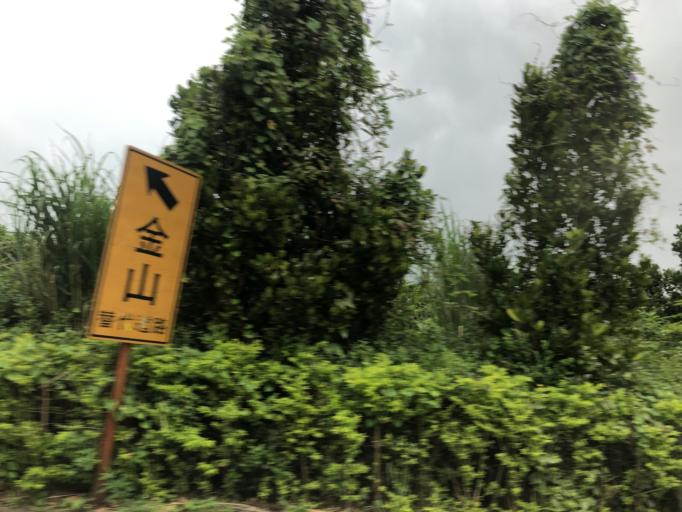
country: TW
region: Taiwan
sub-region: Keelung
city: Keelung
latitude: 25.2147
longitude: 121.6477
